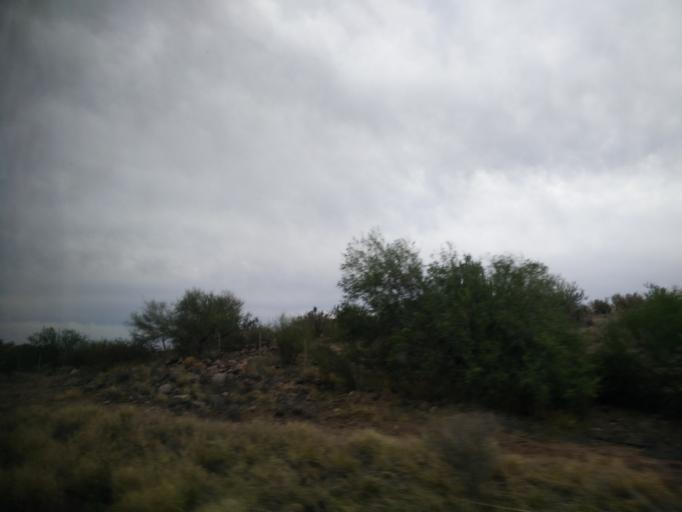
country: MX
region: Sonora
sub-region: Hermosillo
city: Miguel Aleman (La Doce)
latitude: 28.4979
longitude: -111.0433
